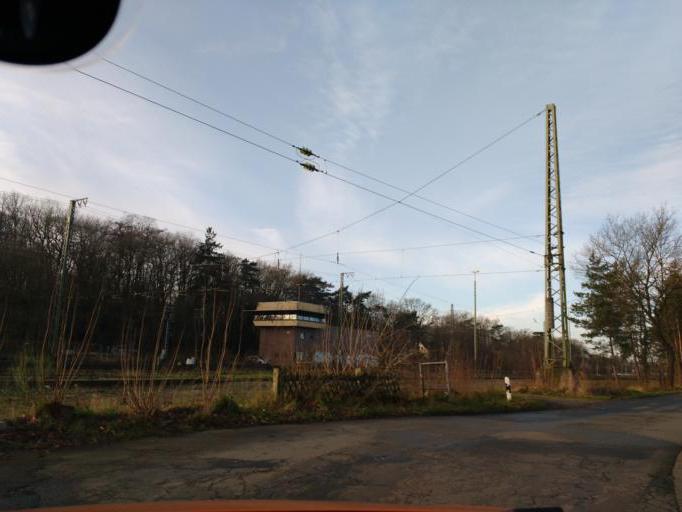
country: DE
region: Lower Saxony
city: Hude
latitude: 53.1071
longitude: 8.4678
